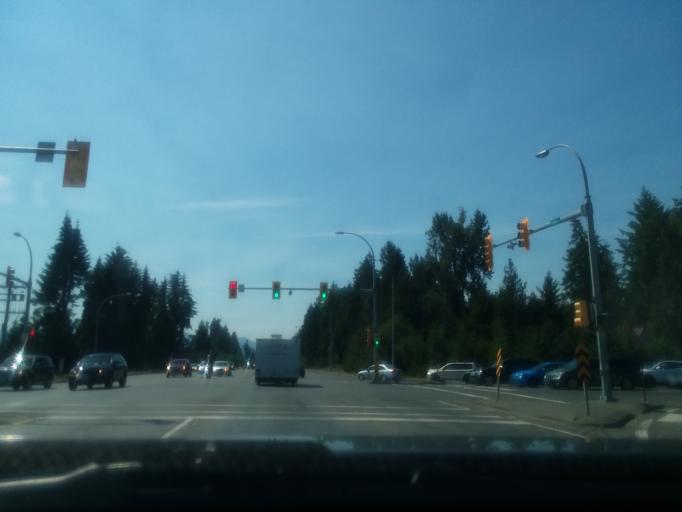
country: CA
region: British Columbia
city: Courtenay
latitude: 49.7106
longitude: -124.9654
